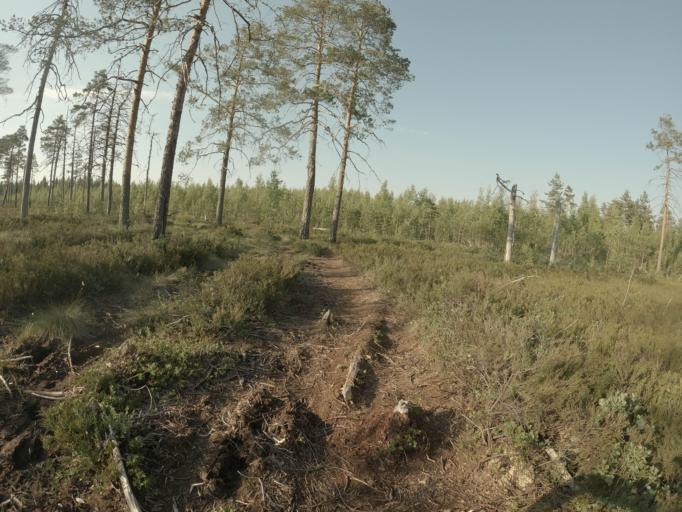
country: RU
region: Leningrad
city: Yakovlevo
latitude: 60.4416
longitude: 29.2401
